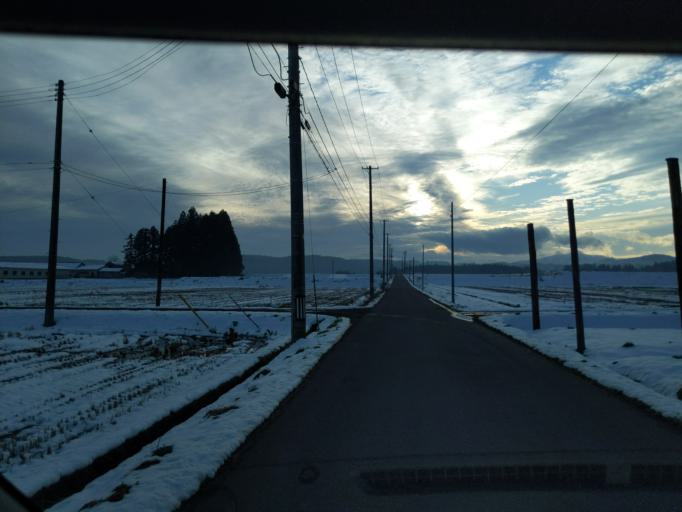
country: JP
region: Iwate
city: Mizusawa
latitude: 39.0623
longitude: 141.0924
